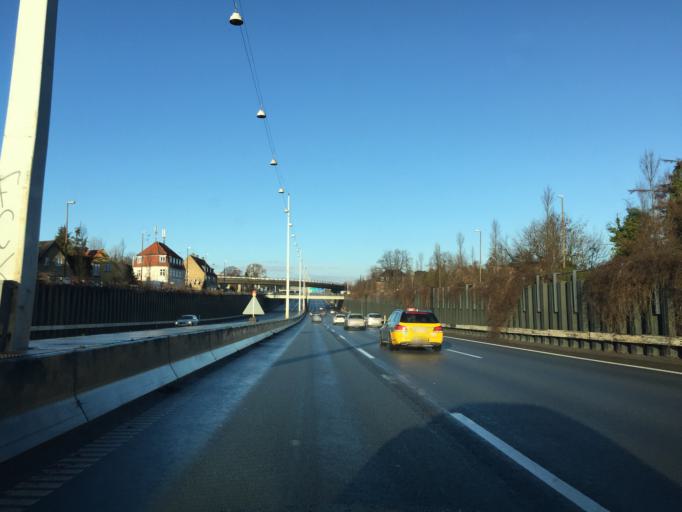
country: DK
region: Capital Region
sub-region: Gentofte Kommune
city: Charlottenlund
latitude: 55.7254
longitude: 12.5530
